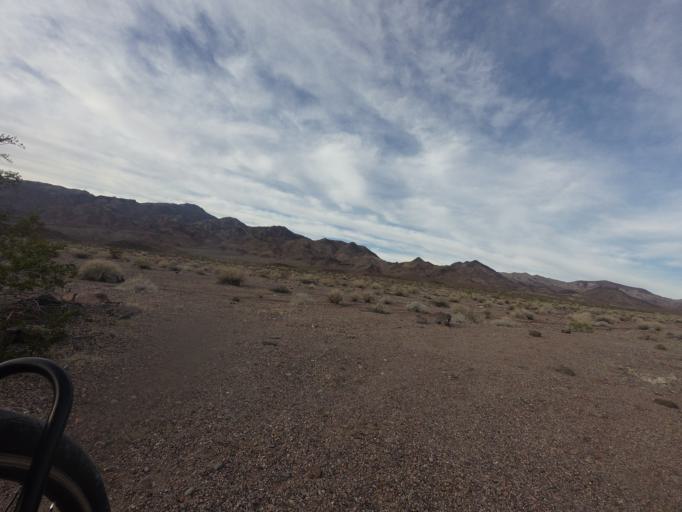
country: US
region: California
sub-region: San Bernardino County
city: Fort Irwin
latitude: 35.9138
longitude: -116.5873
